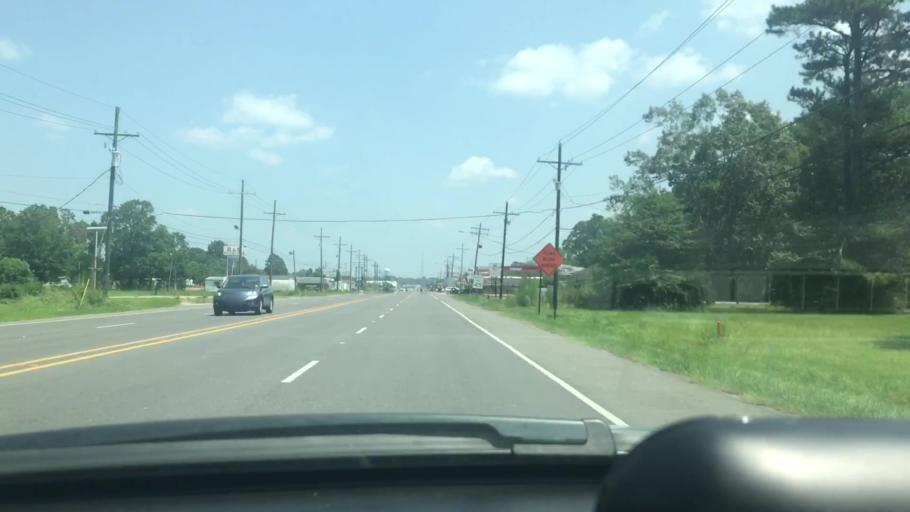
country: US
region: Louisiana
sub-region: Livingston Parish
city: Denham Springs
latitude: 30.4705
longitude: -90.9653
